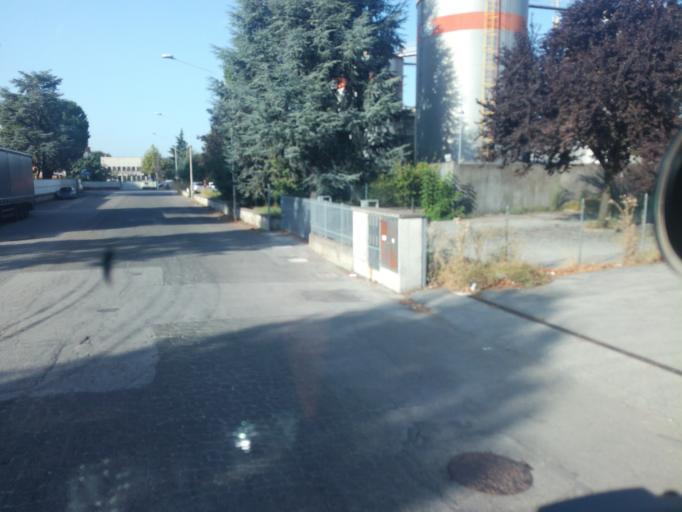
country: IT
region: Emilia-Romagna
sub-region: Provincia di Bologna
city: Progresso
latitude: 44.5512
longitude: 11.3902
